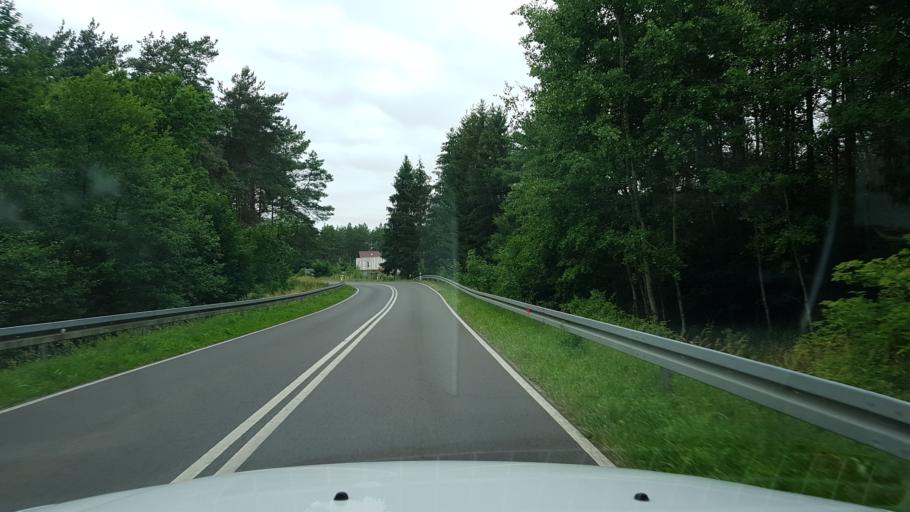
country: PL
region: West Pomeranian Voivodeship
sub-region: Powiat gryficki
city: Brojce
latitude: 53.9534
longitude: 15.3795
